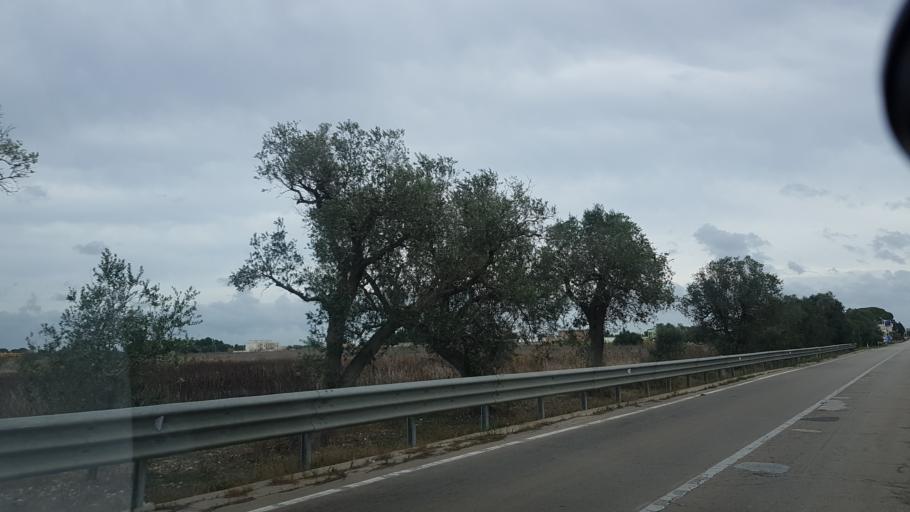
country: IT
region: Apulia
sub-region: Provincia di Lecce
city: Guagnano
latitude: 40.3996
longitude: 17.9351
